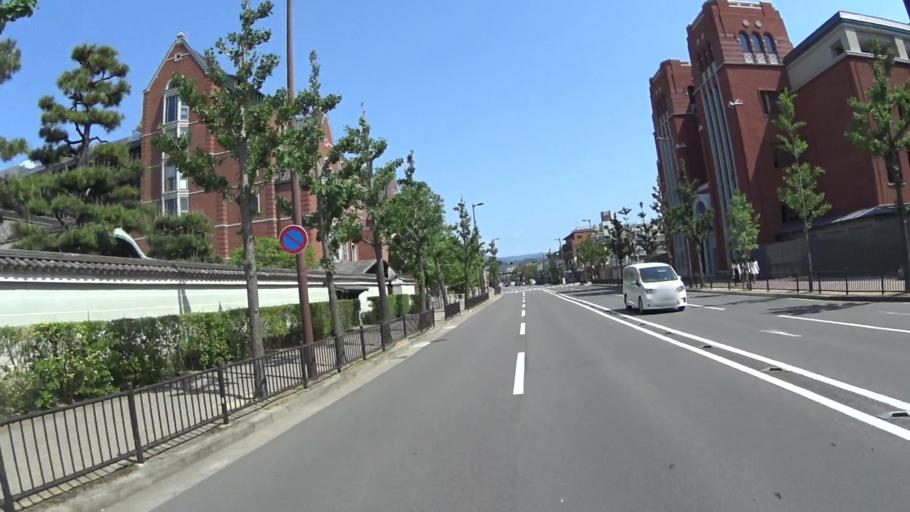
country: JP
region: Kyoto
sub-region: Kyoto-shi
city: Kamigyo-ku
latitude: 35.0307
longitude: 135.7594
